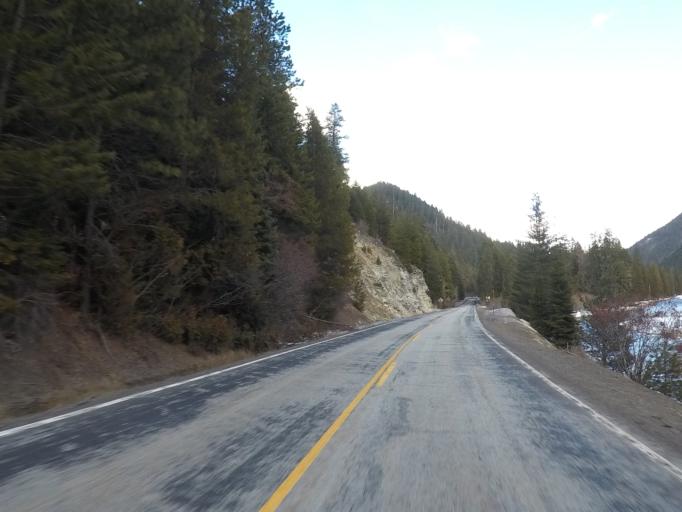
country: US
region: Montana
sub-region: Ravalli County
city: Hamilton
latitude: 46.5106
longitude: -114.7930
